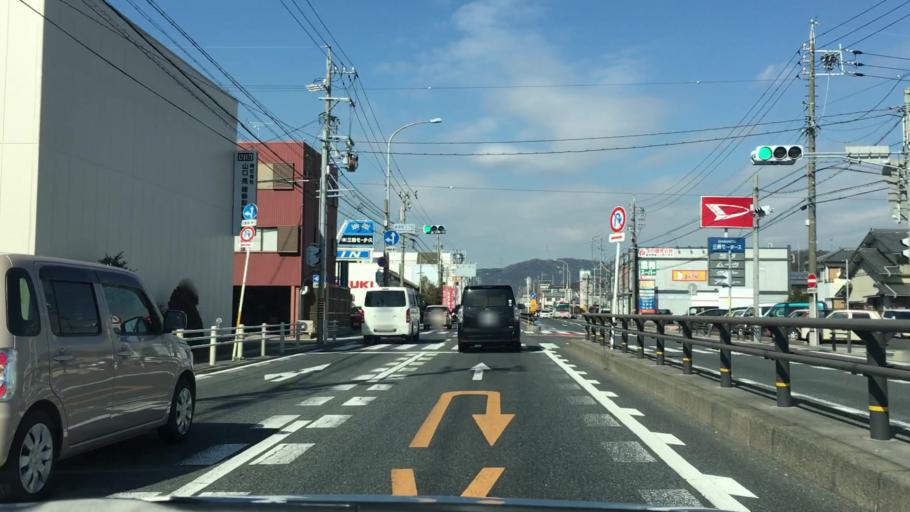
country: JP
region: Aichi
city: Kozakai-cho
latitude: 34.8351
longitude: 137.3282
